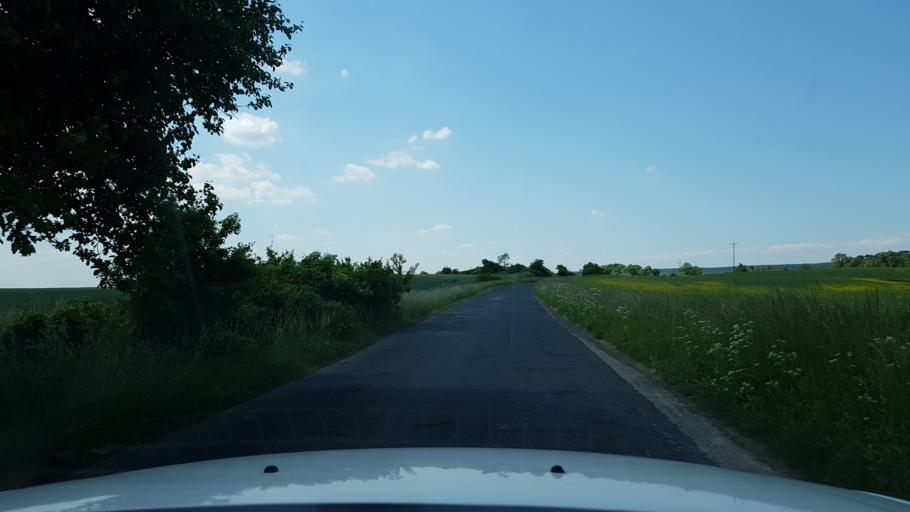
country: PL
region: West Pomeranian Voivodeship
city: Trzcinsko Zdroj
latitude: 52.9944
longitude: 14.5804
